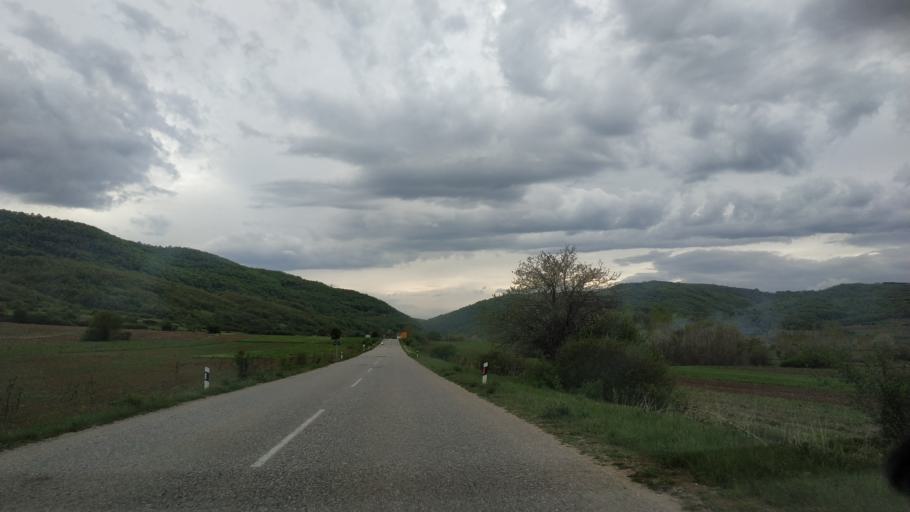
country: RS
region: Central Serbia
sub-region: Zajecarski Okrug
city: Soko Banja
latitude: 43.6545
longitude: 21.7785
